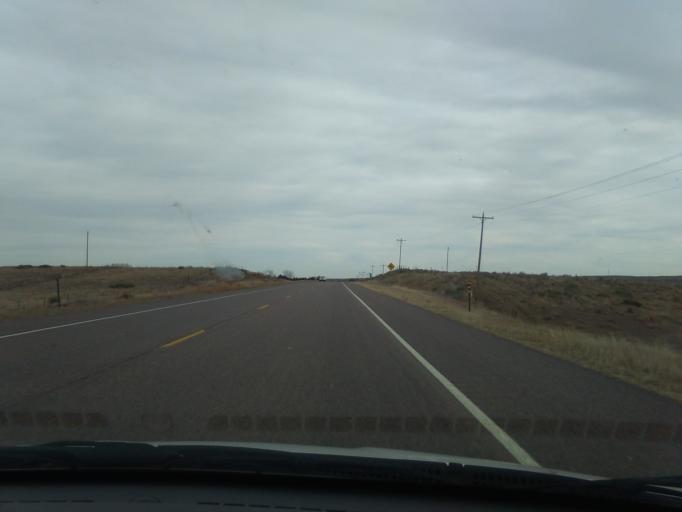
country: US
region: Colorado
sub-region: Yuma County
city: Wray
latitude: 40.0750
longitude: -102.3029
